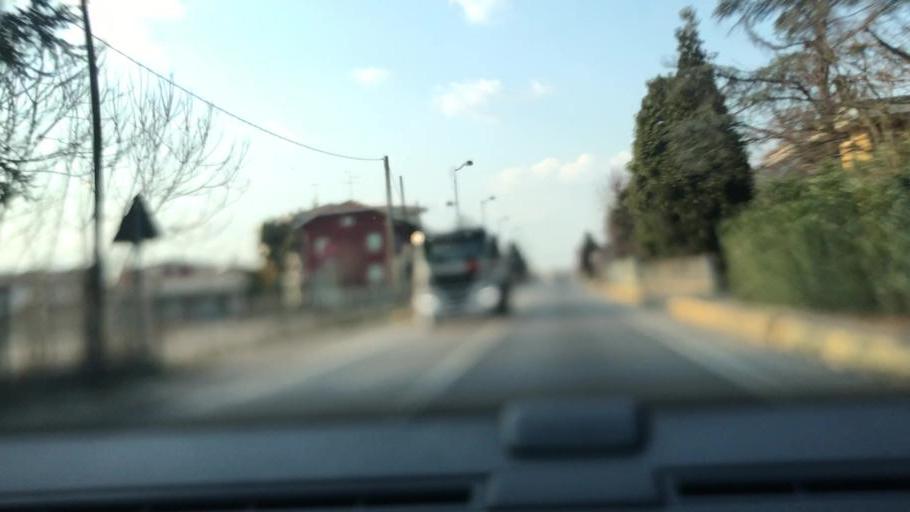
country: IT
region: Emilia-Romagna
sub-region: Provincia di Parma
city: Mezzano Inferiore
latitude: 44.9440
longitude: 10.4777
